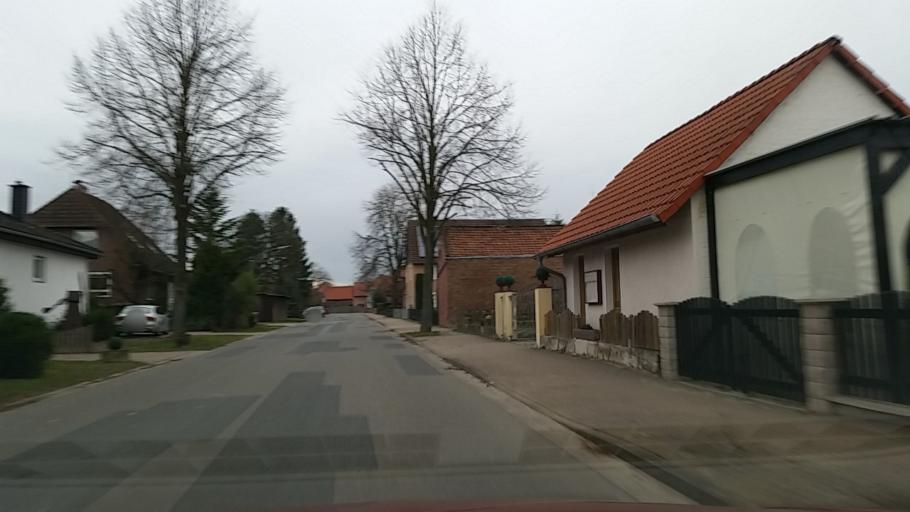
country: DE
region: Lower Saxony
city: Wasbuttel
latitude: 52.3591
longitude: 10.5955
